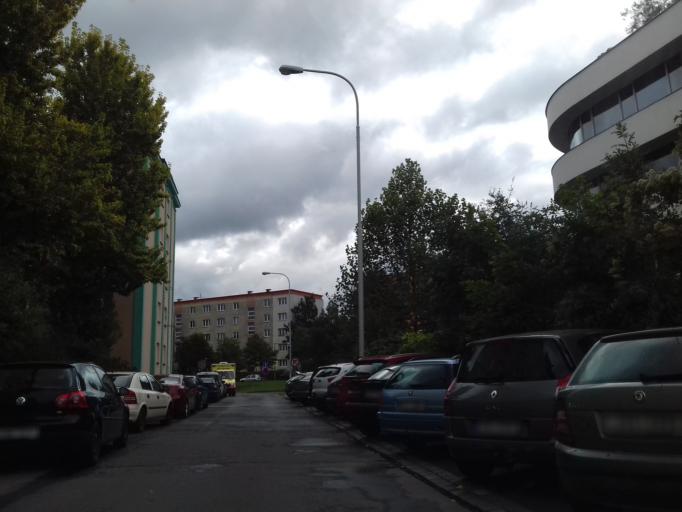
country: CZ
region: Praha
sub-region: Praha 4
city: Hodkovicky
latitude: 50.0445
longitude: 14.4439
